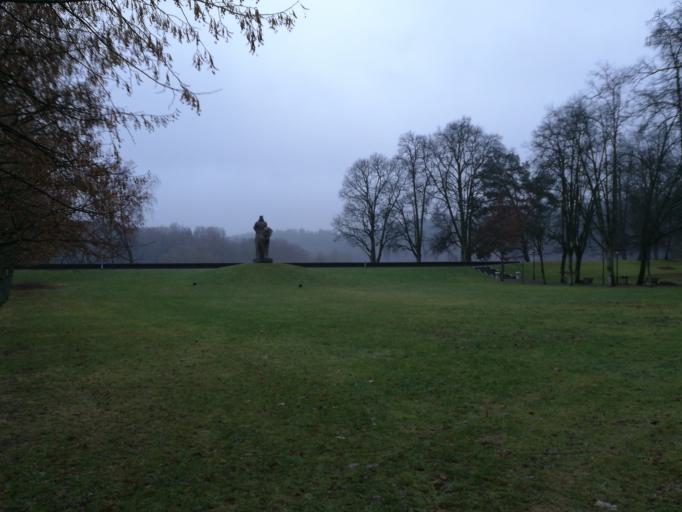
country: LT
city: Birstonas
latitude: 54.5985
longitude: 24.0341
